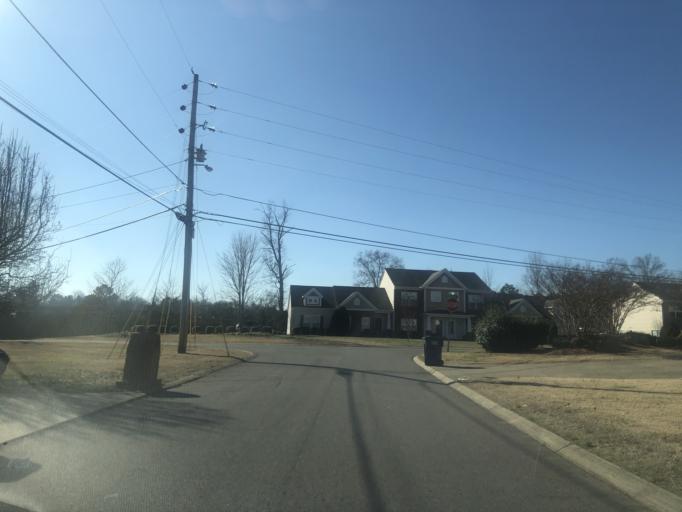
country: US
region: Tennessee
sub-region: Rutherford County
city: Smyrna
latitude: 35.9407
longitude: -86.5344
